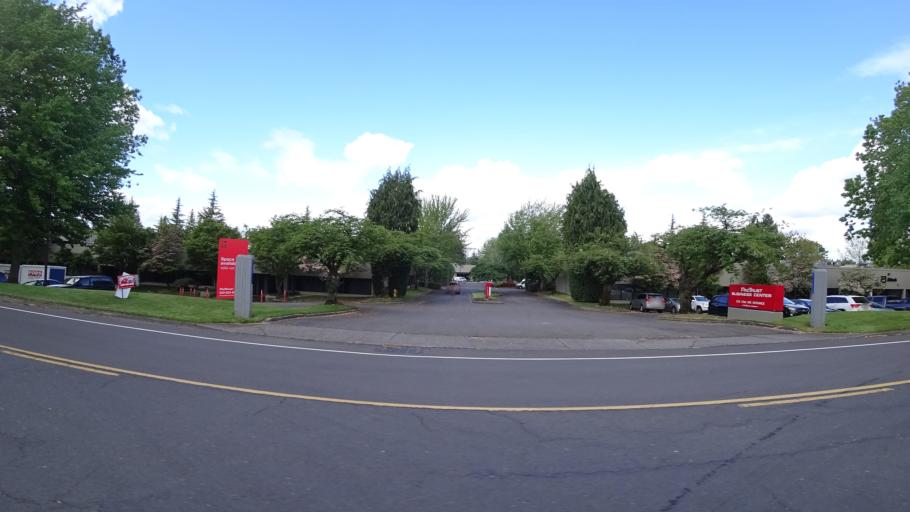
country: US
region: Oregon
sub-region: Washington County
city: Durham
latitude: 45.4021
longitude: -122.7491
